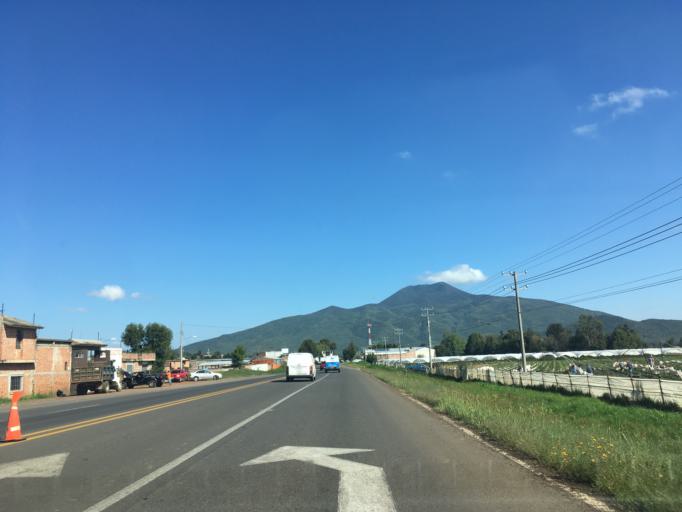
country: MX
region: Mexico
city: Tangancicuaro de Arista
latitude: 19.8795
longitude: -102.1989
